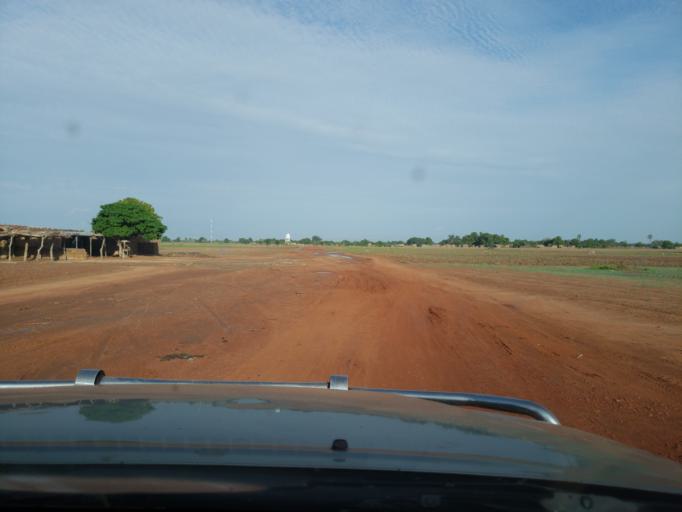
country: ML
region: Sikasso
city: Koutiala
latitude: 12.4236
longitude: -5.6703
